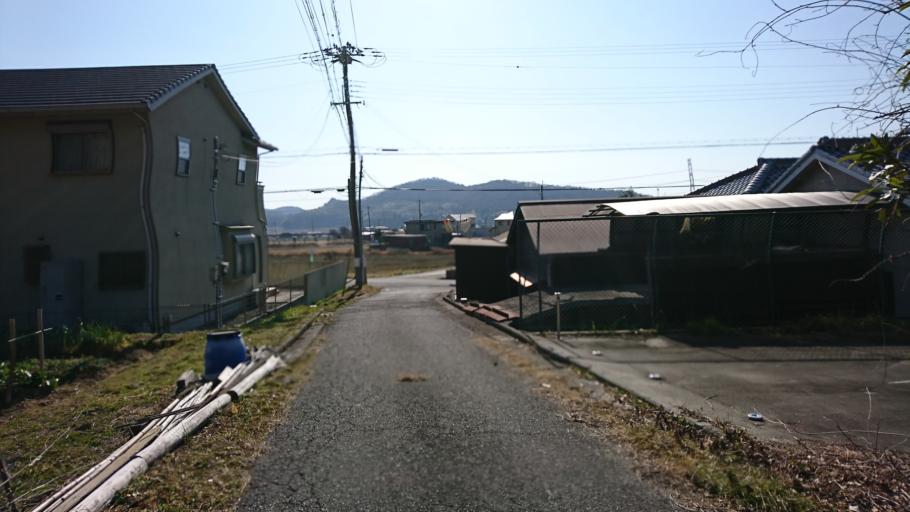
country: JP
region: Hyogo
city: Kakogawacho-honmachi
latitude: 34.8304
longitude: 134.8458
